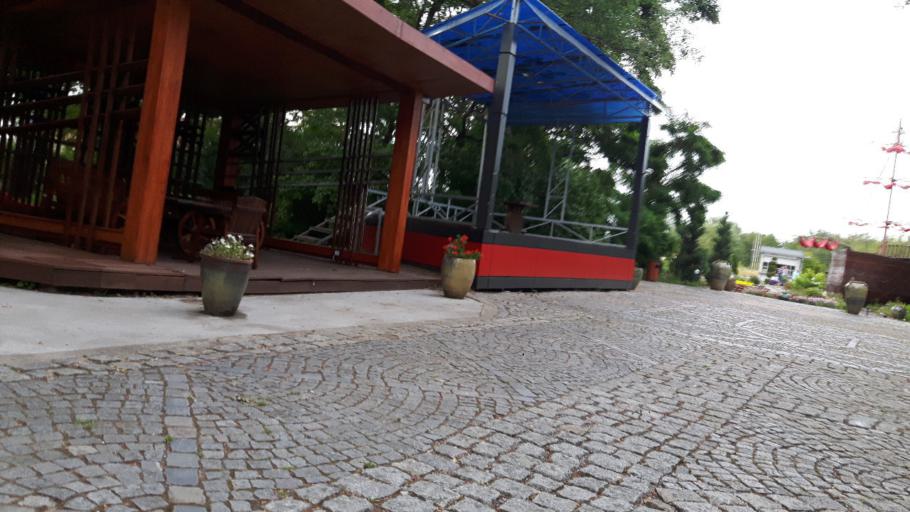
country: RU
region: Kaliningrad
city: Vzmorye
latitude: 54.6523
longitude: 20.3595
